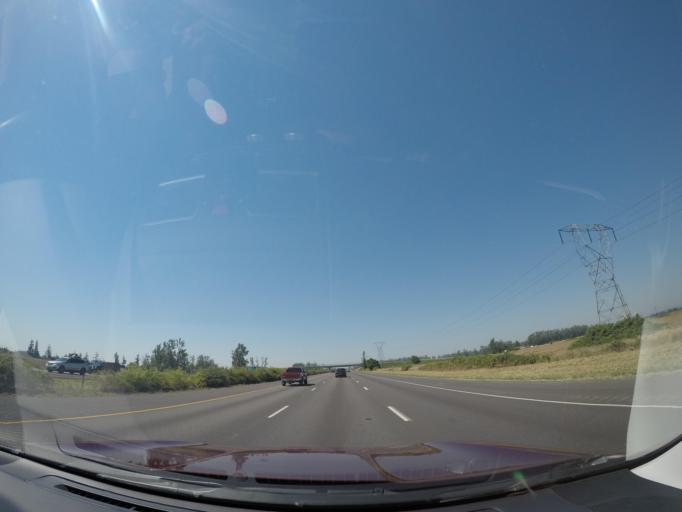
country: US
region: Oregon
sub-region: Marion County
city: Gervais
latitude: 45.1182
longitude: -122.9145
